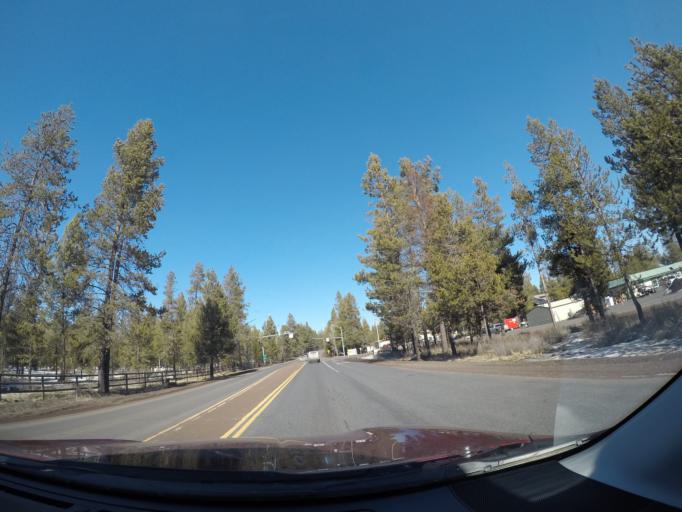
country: US
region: Oregon
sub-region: Deschutes County
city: Sunriver
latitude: 43.8655
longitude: -121.4371
